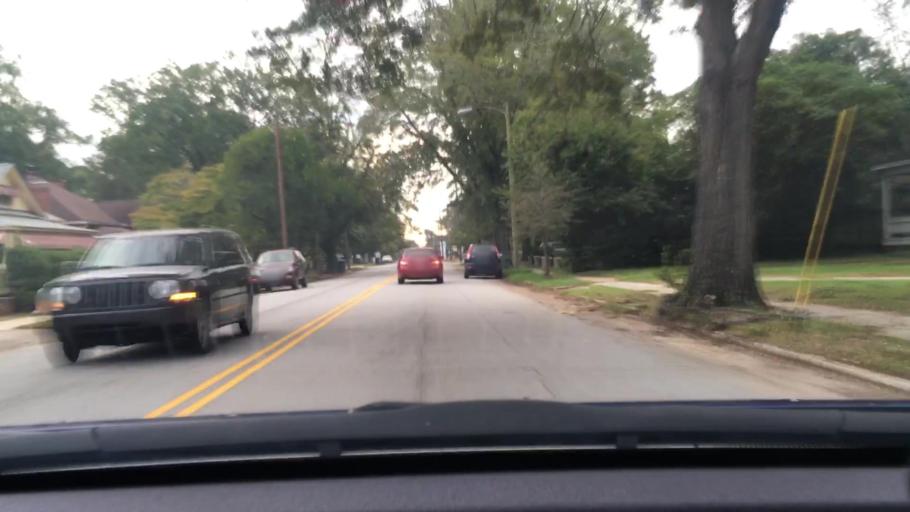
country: US
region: South Carolina
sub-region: Richland County
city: Columbia
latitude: 34.0239
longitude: -81.0482
